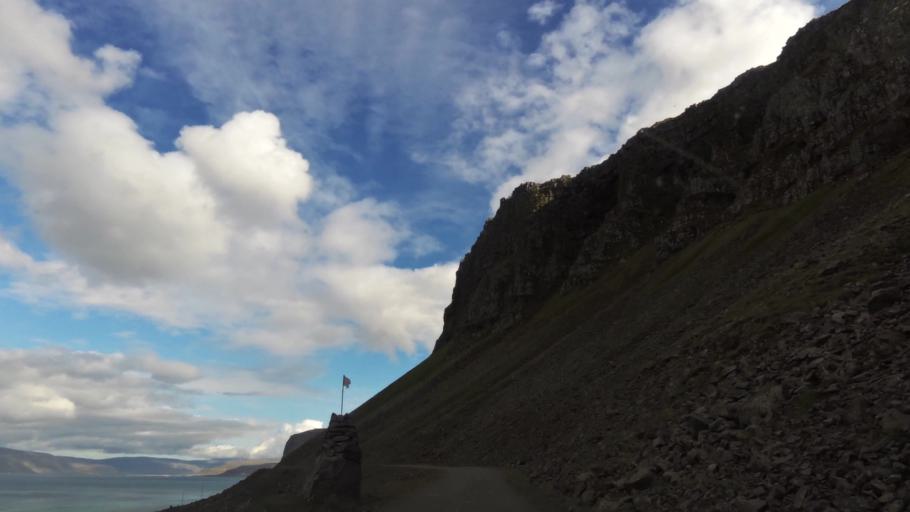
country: IS
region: West
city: Olafsvik
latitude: 65.6012
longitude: -24.1426
